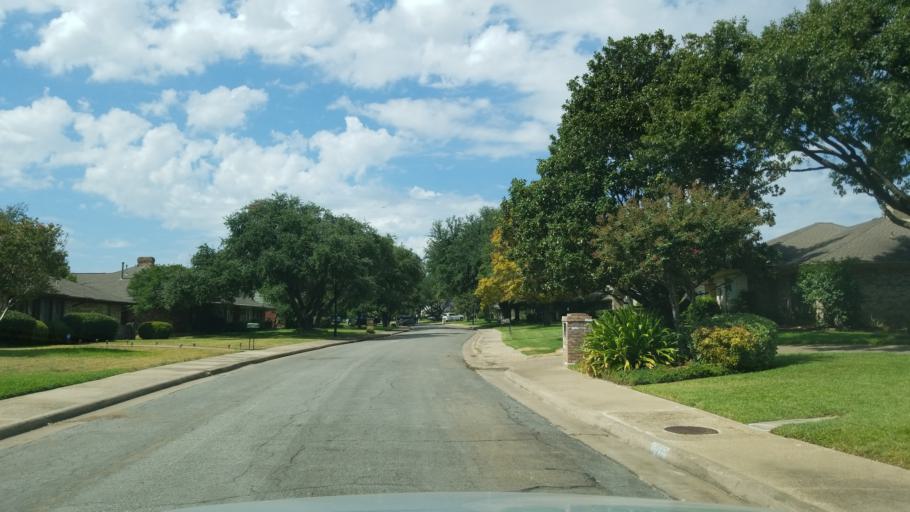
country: US
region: Texas
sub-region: Dallas County
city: Addison
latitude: 32.9586
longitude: -96.7799
